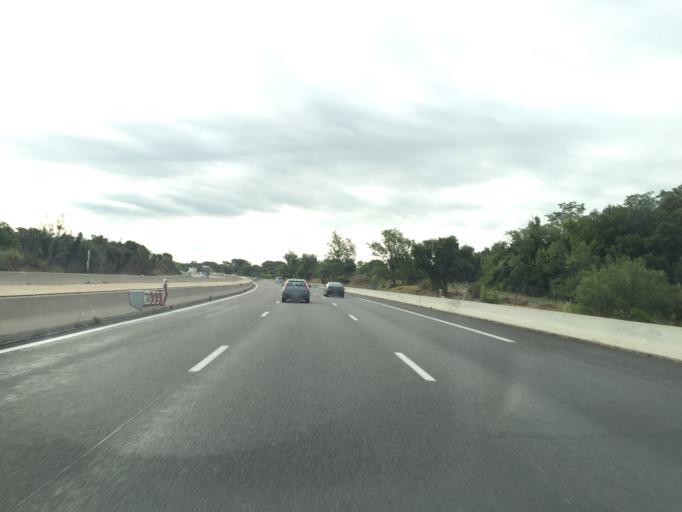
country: FR
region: Provence-Alpes-Cote d'Azur
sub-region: Departement du Var
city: Le Muy
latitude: 43.4590
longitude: 6.6011
